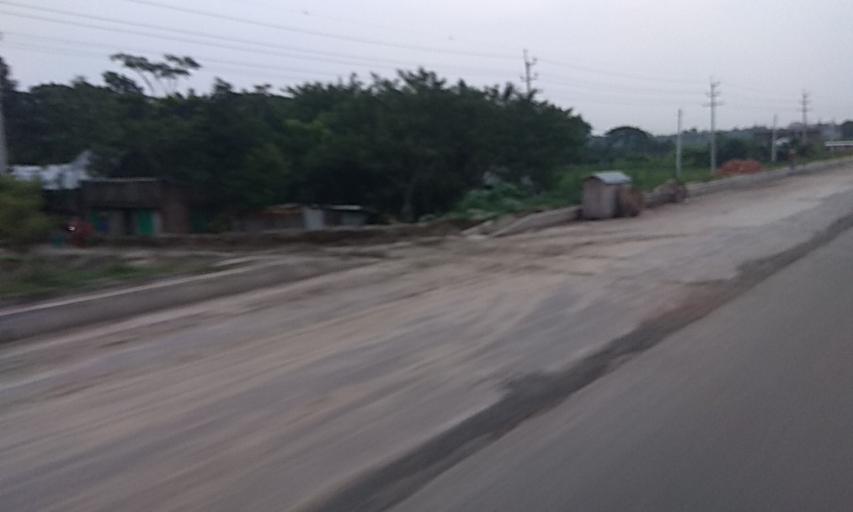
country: BD
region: Dhaka
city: Char Bhadrasan
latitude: 23.3747
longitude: 90.0246
